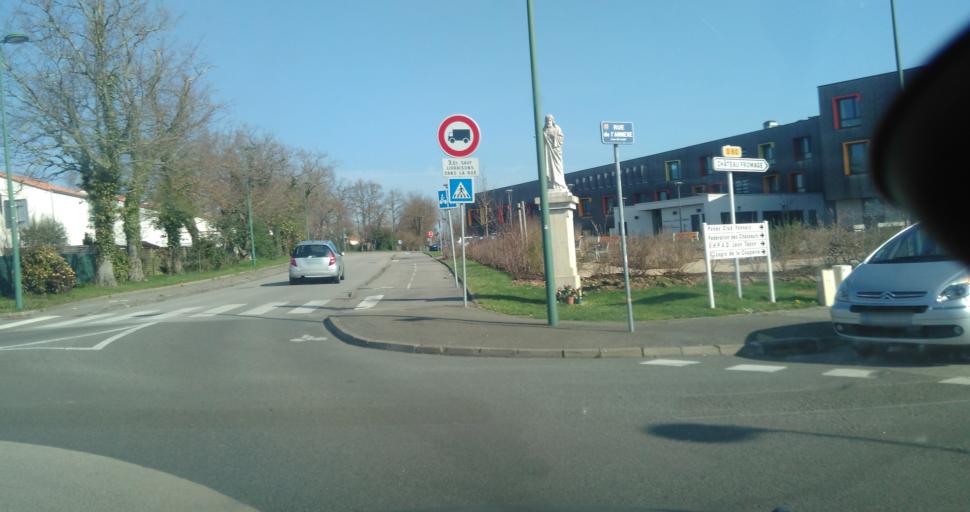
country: FR
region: Pays de la Loire
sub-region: Departement de la Vendee
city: La Roche-sur-Yon
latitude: 46.6657
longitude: -1.3986
